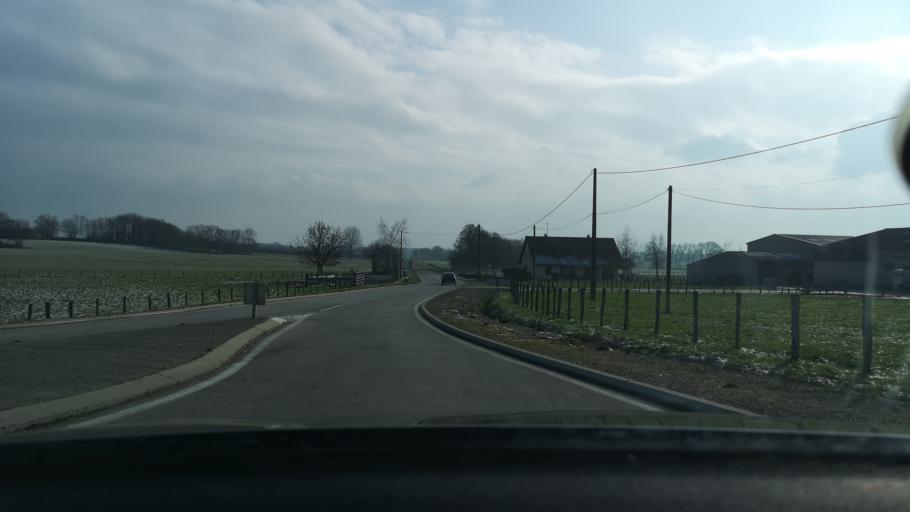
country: FR
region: Bourgogne
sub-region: Departement de Saone-et-Loire
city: Saint-Usuge
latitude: 46.7156
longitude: 5.3132
